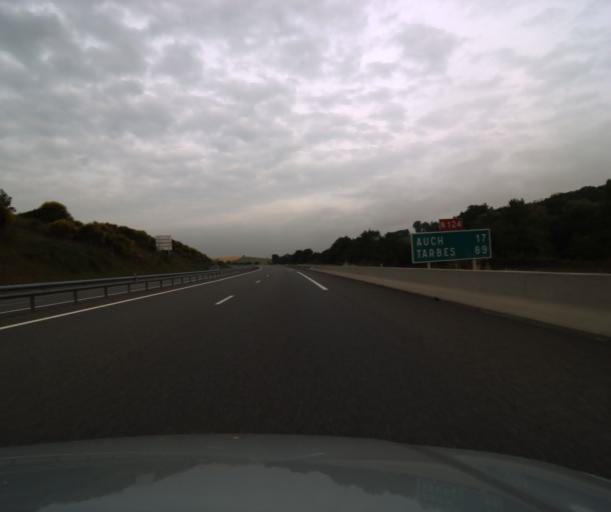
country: FR
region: Midi-Pyrenees
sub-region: Departement du Gers
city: Aubiet
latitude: 43.6590
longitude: 0.7732
